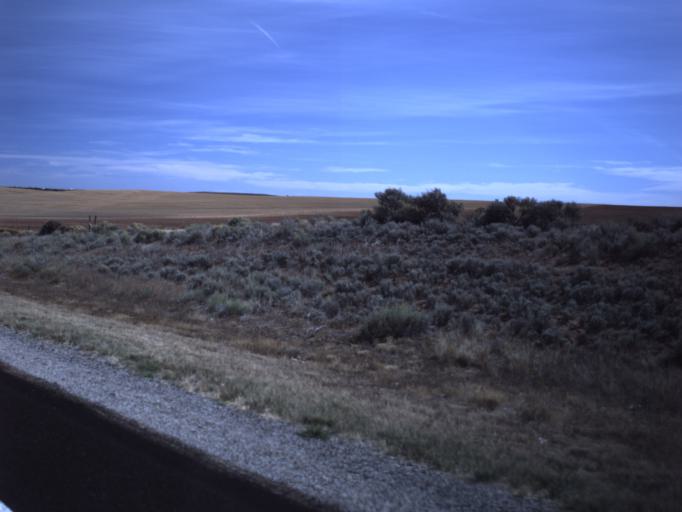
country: US
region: Colorado
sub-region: Dolores County
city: Dove Creek
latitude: 37.8166
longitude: -109.0427
